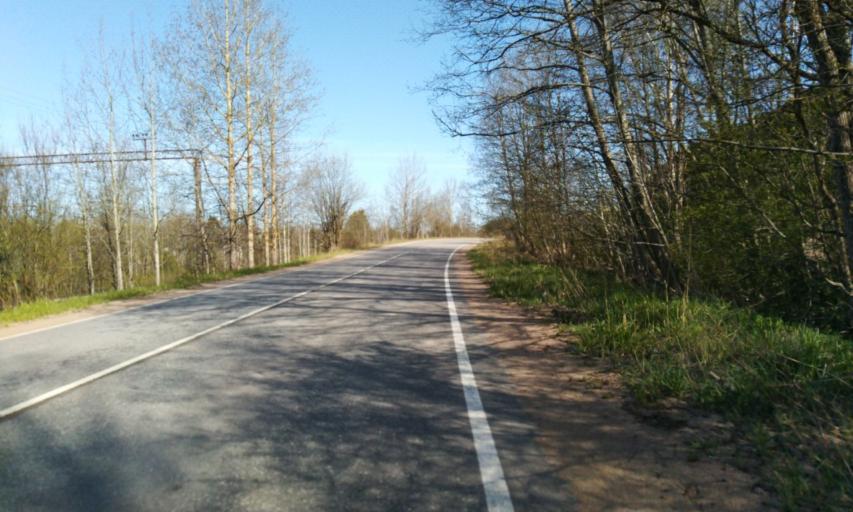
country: RU
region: Leningrad
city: Leskolovo
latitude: 60.3276
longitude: 30.4249
